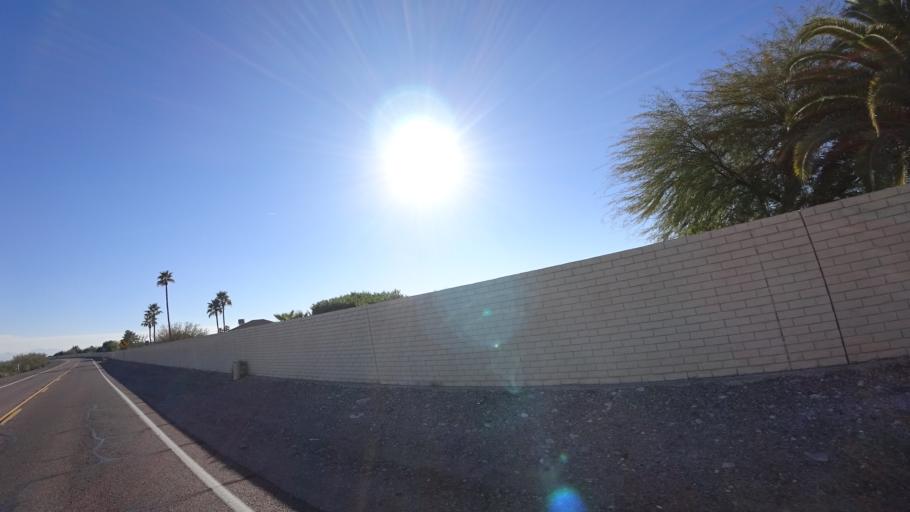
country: US
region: Arizona
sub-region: Maricopa County
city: Sun City West
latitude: 33.6659
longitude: -112.3256
